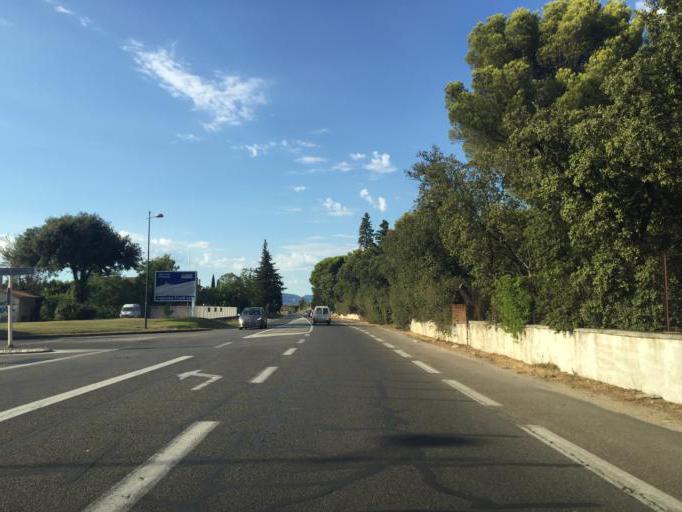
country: FR
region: Provence-Alpes-Cote d'Azur
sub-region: Departement du Vaucluse
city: Carpentras
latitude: 44.0262
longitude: 5.0523
